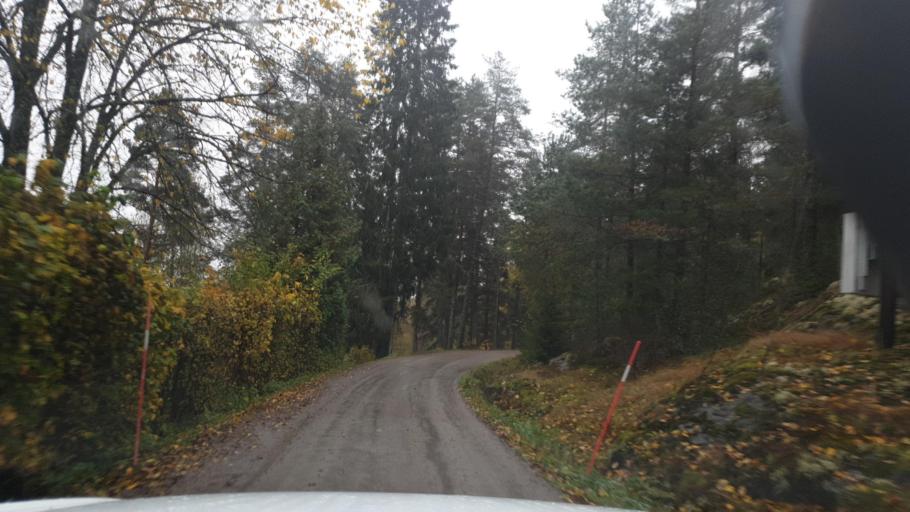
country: SE
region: Vaermland
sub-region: Eda Kommun
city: Amotfors
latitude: 59.7339
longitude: 12.2783
